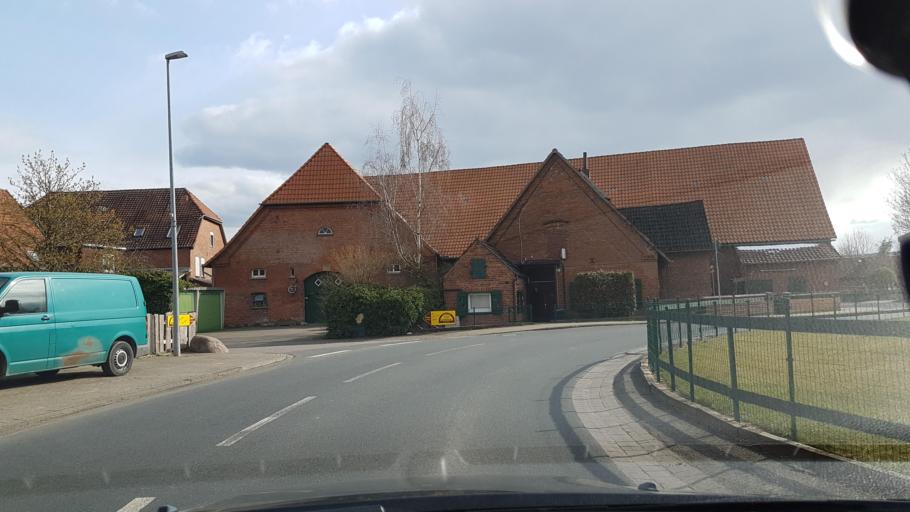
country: DE
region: Lower Saxony
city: Gehrden
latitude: 52.3204
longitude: 9.5517
